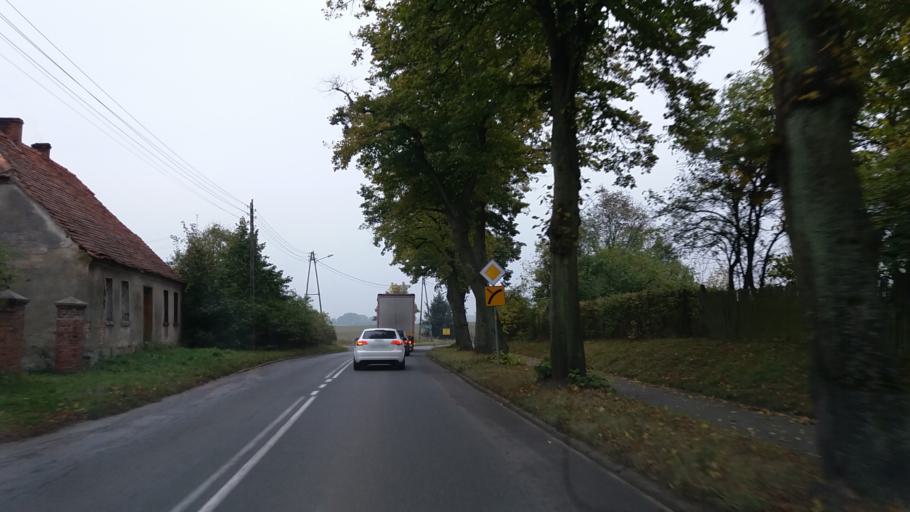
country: PL
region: West Pomeranian Voivodeship
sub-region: Powiat choszczenski
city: Bierzwnik
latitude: 53.0446
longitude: 15.6685
